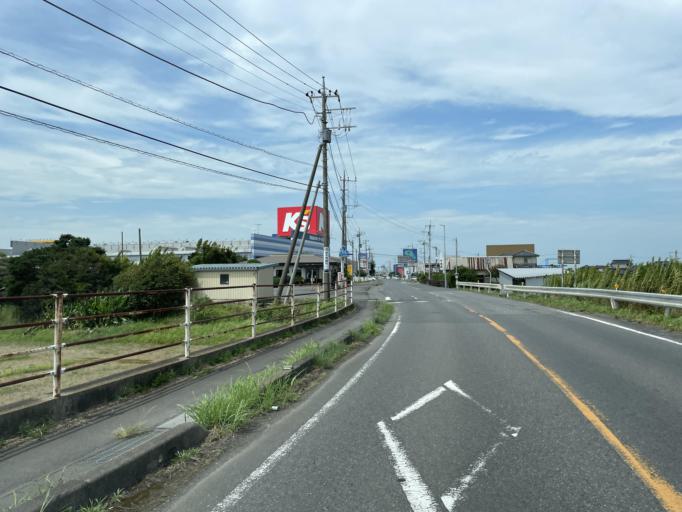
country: JP
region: Chiba
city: Katori-shi
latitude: 35.9167
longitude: 140.4901
